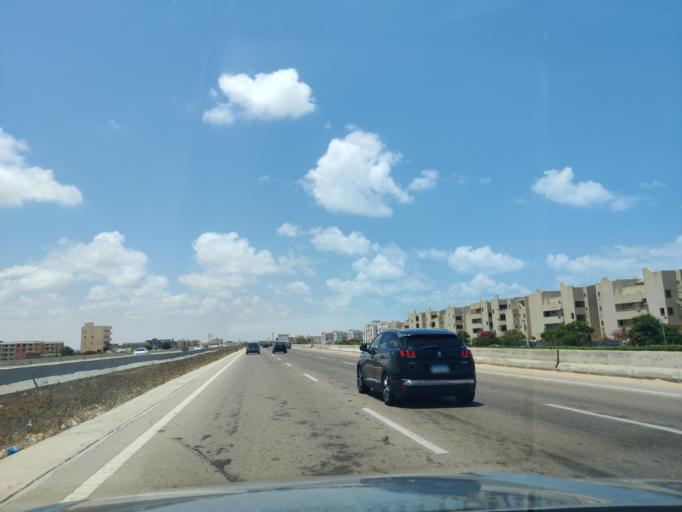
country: EG
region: Muhafazat Matruh
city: Al `Alamayn
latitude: 30.8377
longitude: 29.2447
